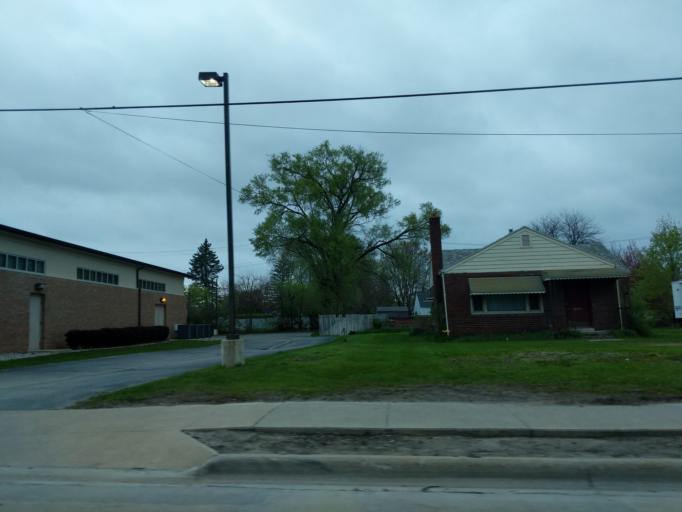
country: US
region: Michigan
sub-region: Tuscola County
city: Vassar
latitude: 43.3724
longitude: -83.5885
